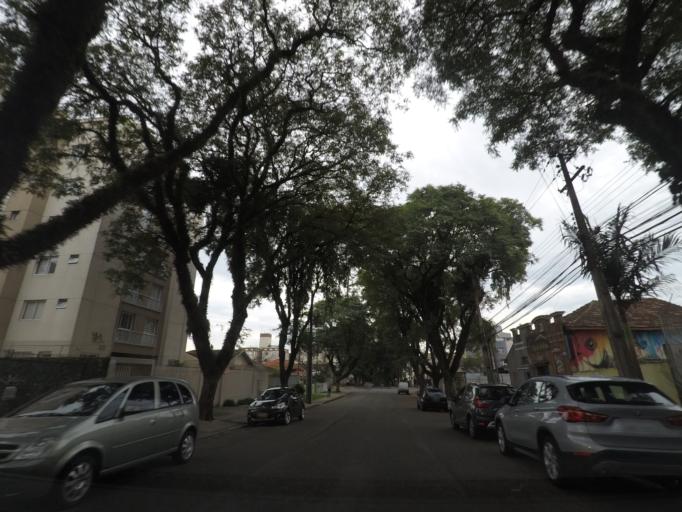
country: BR
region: Parana
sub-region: Curitiba
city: Curitiba
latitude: -25.4808
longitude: -49.2975
